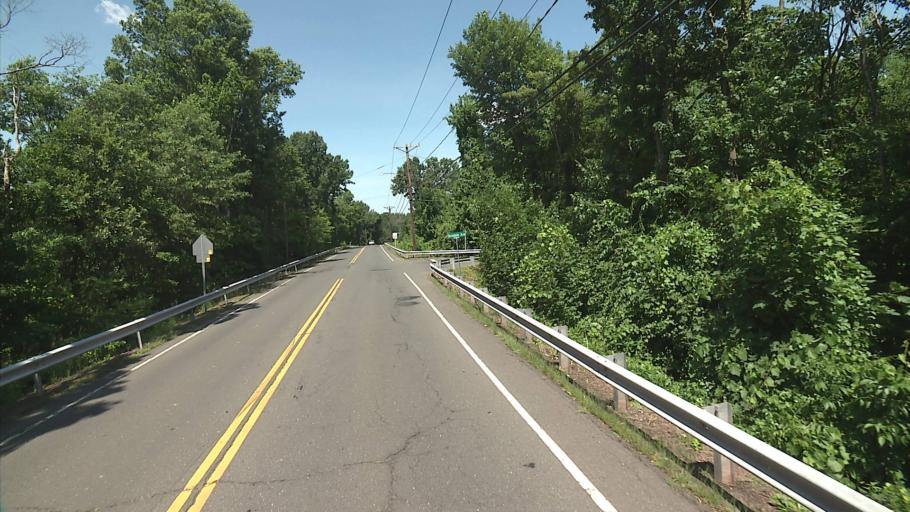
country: US
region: Connecticut
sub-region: Hartford County
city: Kensington
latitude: 41.6372
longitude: -72.7733
